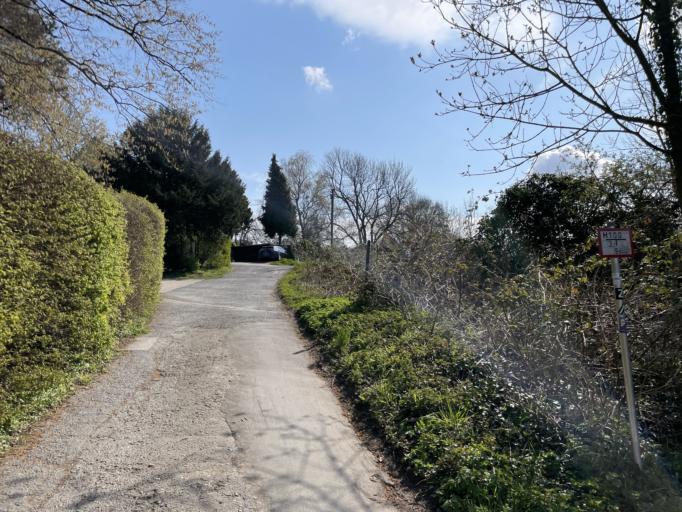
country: DE
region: North Rhine-Westphalia
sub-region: Regierungsbezirk Dusseldorf
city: Muelheim (Ruhr)
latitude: 51.4225
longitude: 6.9226
